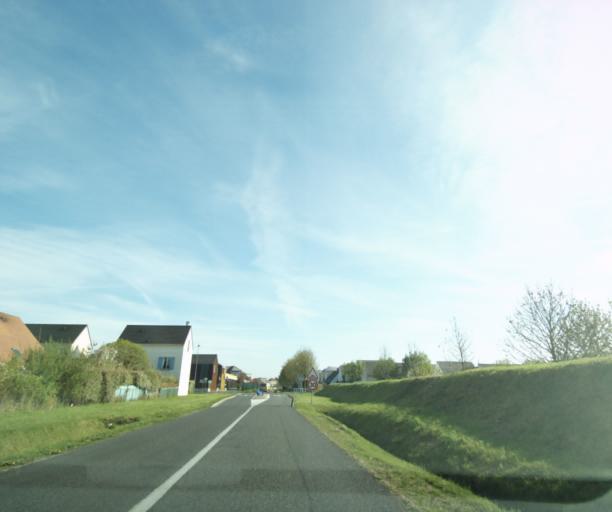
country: FR
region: Ile-de-France
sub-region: Departement de Seine-et-Marne
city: Nangis
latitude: 48.5528
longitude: 3.0030
